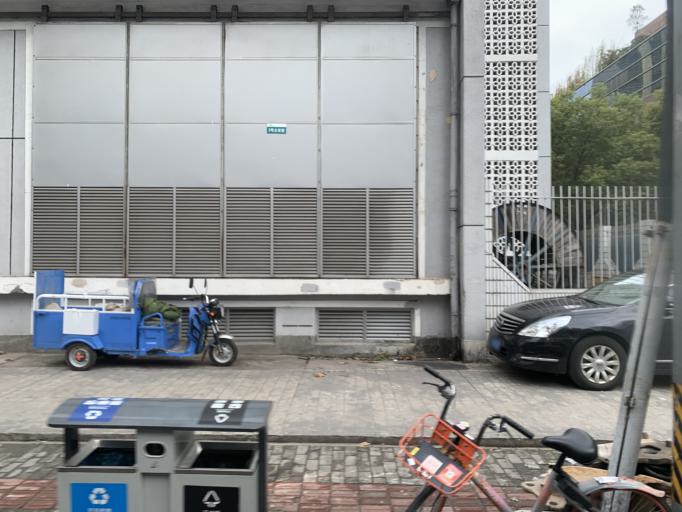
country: CN
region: Shanghai Shi
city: Pudong
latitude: 31.2302
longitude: 121.5185
